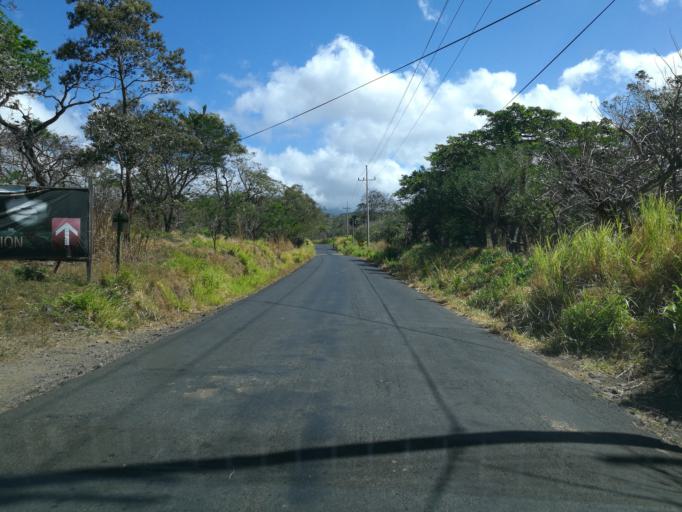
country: CR
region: Guanacaste
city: Liberia
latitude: 10.7303
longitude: -85.3897
